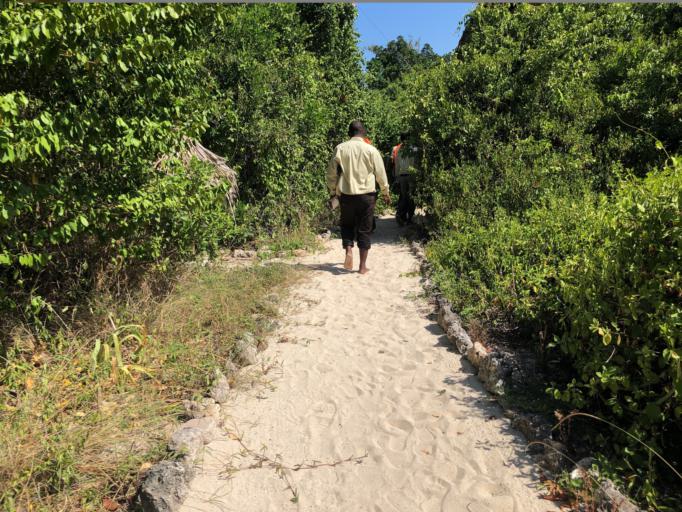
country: TZ
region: Zanzibar Urban/West
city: Zanzibar
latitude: -6.2808
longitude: 39.1771
